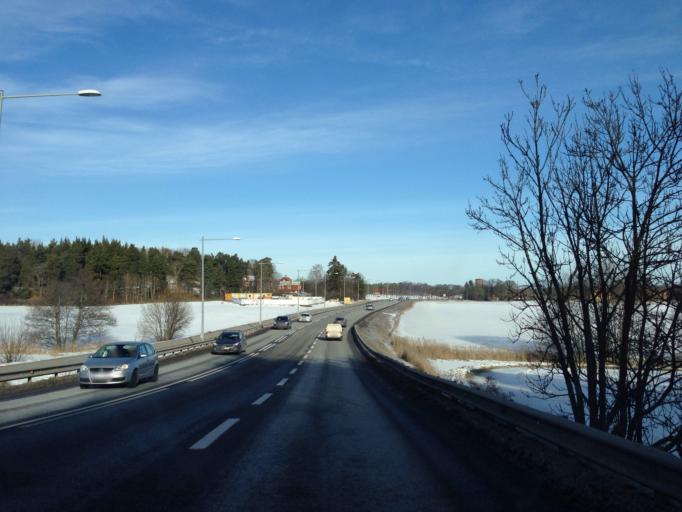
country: SE
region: Stockholm
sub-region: Ekero Kommun
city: Ekeroe
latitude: 59.3140
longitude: 17.8608
